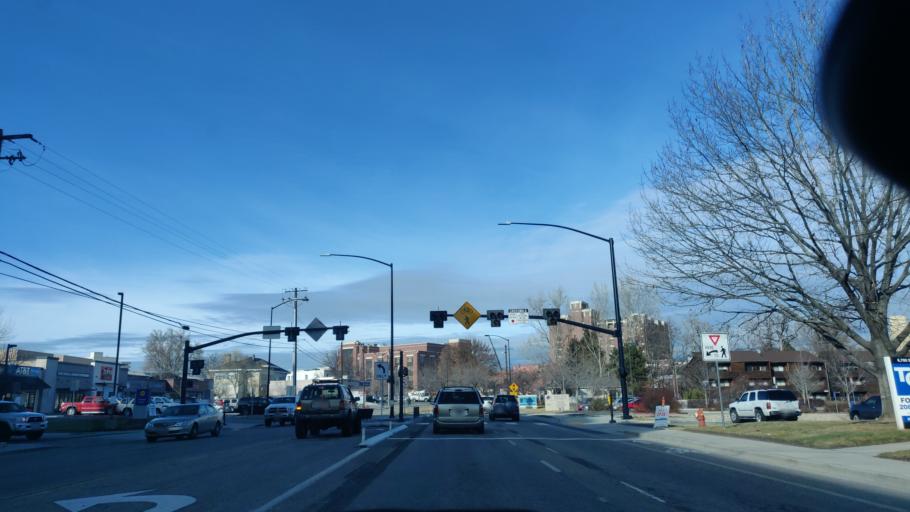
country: US
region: Idaho
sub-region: Ada County
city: Boise
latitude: 43.6091
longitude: -116.1934
